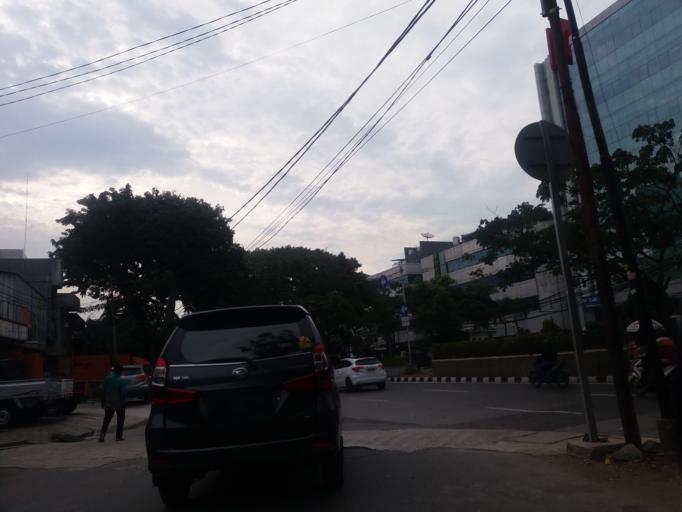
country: ID
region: Jakarta Raya
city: Jakarta
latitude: -6.1444
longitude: 106.8316
